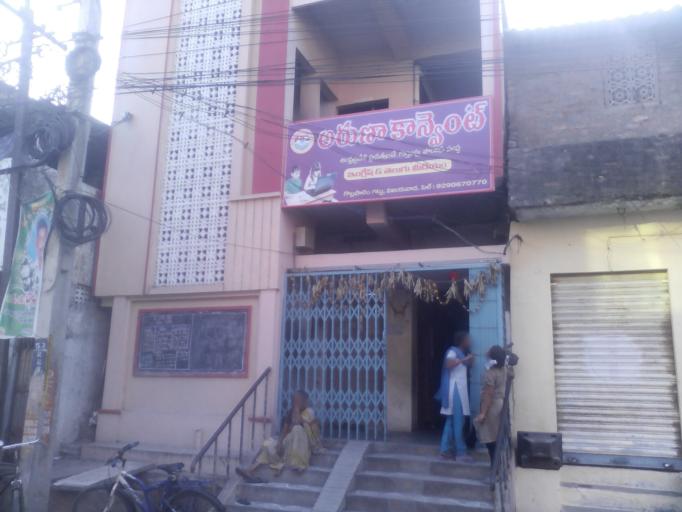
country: IN
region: Andhra Pradesh
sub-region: Krishna
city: Vijayawada
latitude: 16.5278
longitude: 80.6123
